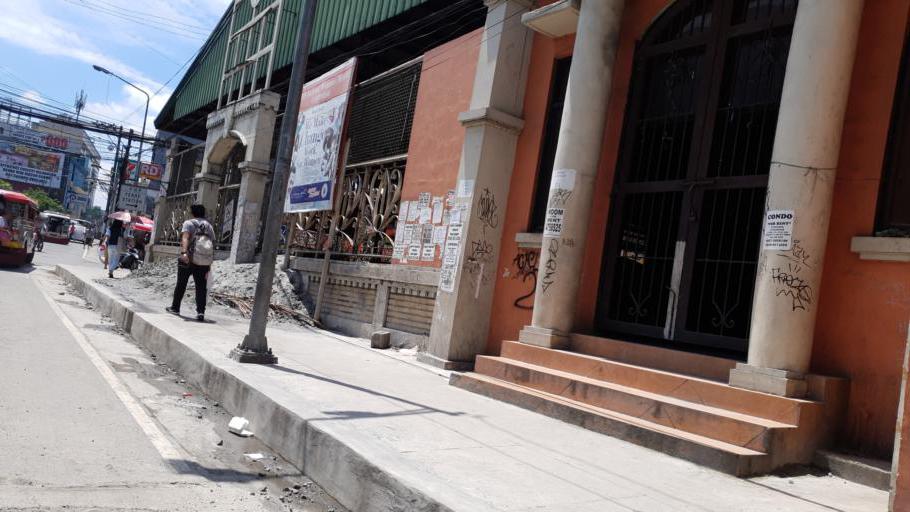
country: PH
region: Metro Manila
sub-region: San Juan
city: San Juan
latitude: 14.6011
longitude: 121.0130
